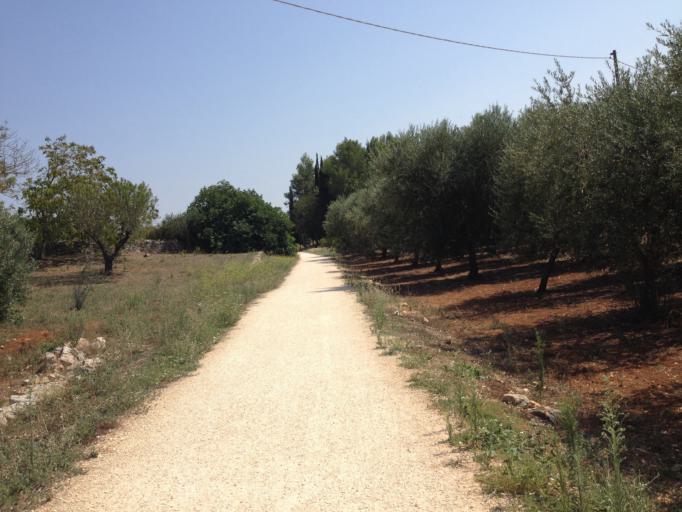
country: IT
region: Apulia
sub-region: Provincia di Brindisi
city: Cisternino
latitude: 40.7188
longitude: 17.4024
